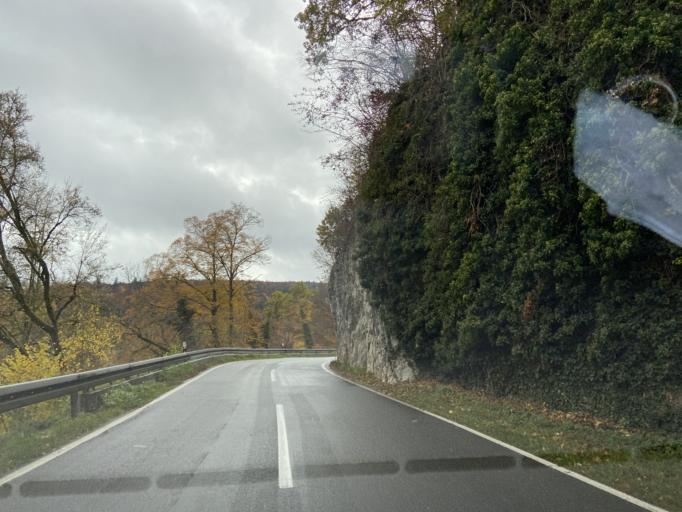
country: DE
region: Baden-Wuerttemberg
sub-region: Tuebingen Region
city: Inzigkofen
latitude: 48.0823
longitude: 9.1274
